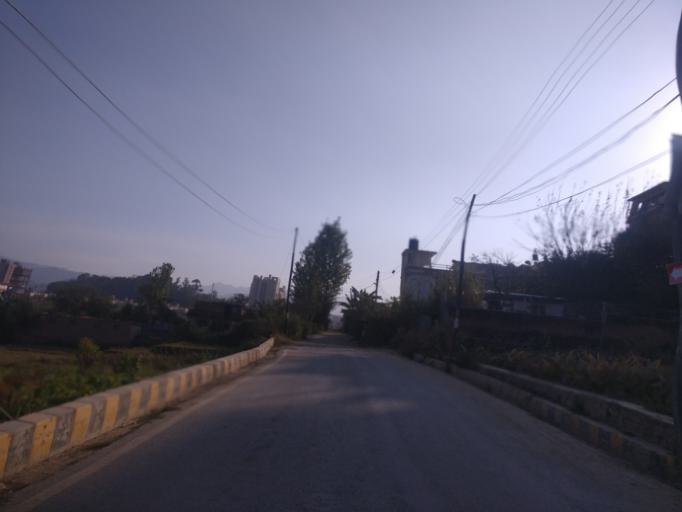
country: NP
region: Central Region
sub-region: Bagmati Zone
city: Patan
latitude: 27.6551
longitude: 85.3330
